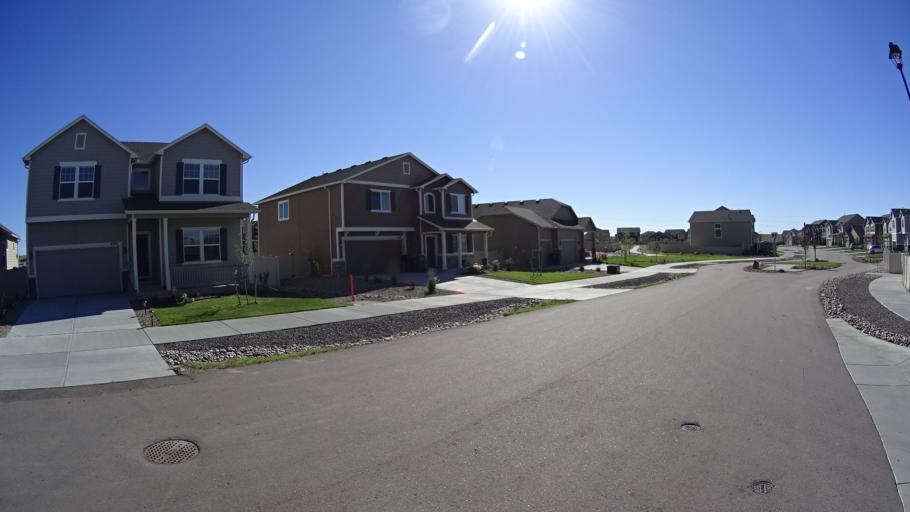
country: US
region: Colorado
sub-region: El Paso County
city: Cimarron Hills
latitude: 38.8956
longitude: -104.6756
